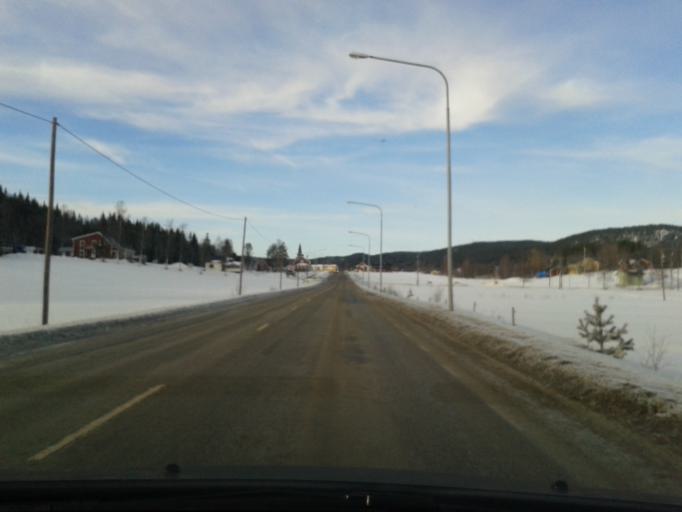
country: SE
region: Vaesternorrland
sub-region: OErnskoeldsviks Kommun
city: Bredbyn
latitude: 63.5076
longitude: 18.0701
